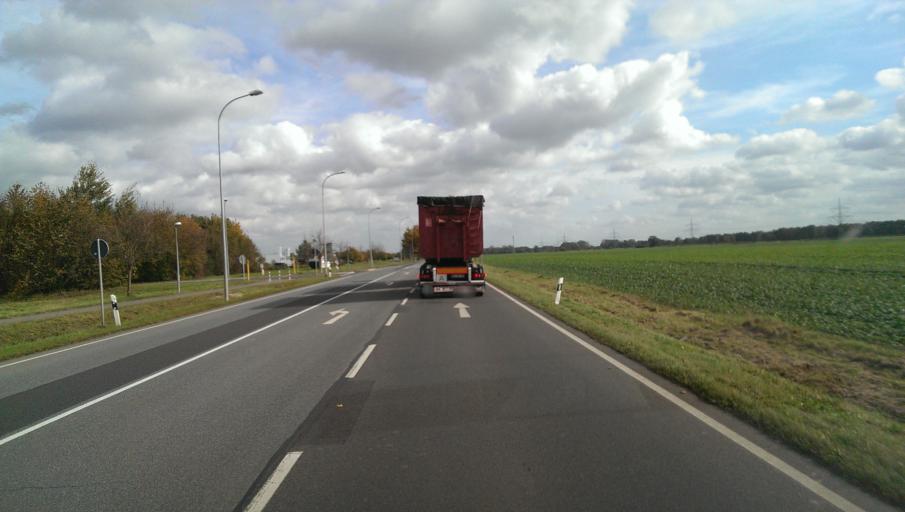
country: DE
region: Brandenburg
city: Schwarzheide
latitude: 51.4707
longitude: 13.8228
